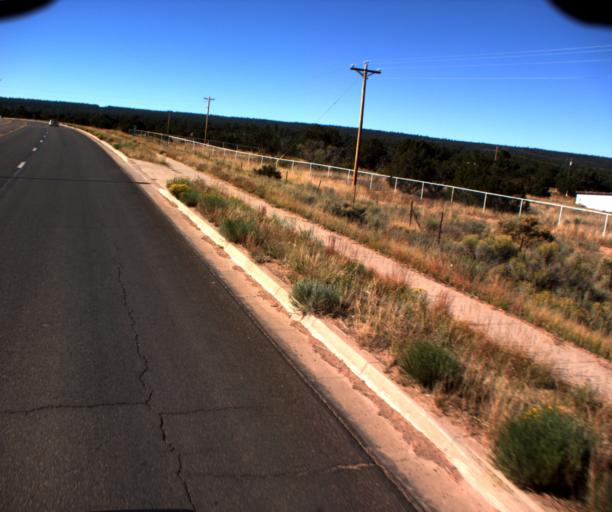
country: US
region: Arizona
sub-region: Apache County
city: Saint Michaels
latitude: 35.6591
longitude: -109.1161
